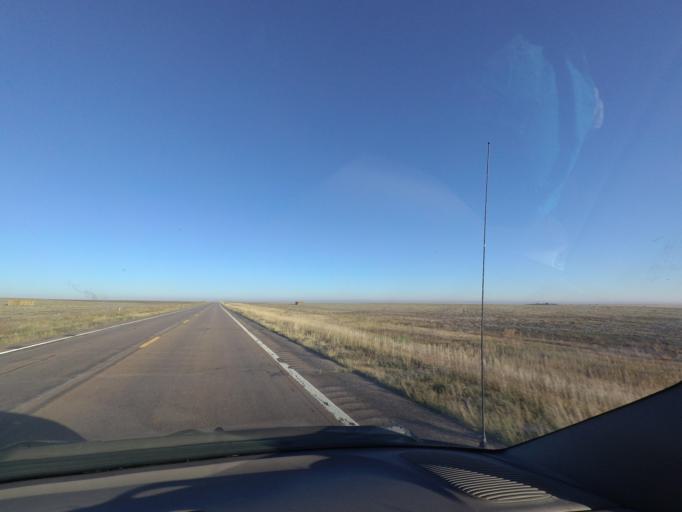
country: US
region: Colorado
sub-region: Washington County
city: Akron
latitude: 39.7326
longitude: -103.1678
